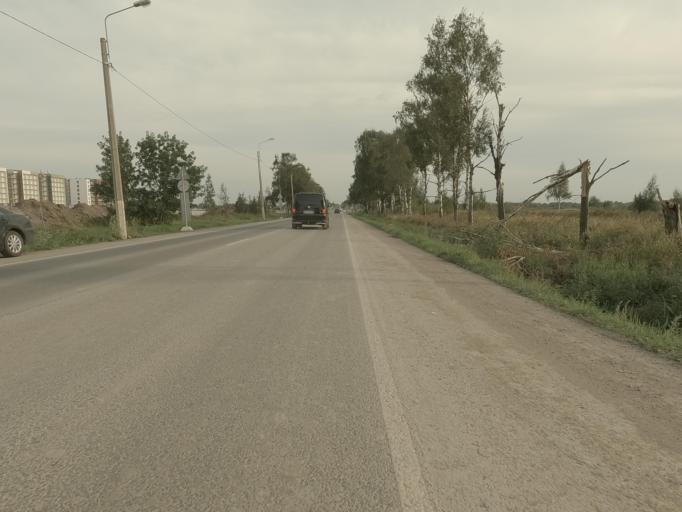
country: RU
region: St.-Petersburg
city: Strel'na
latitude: 59.8450
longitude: 30.0909
